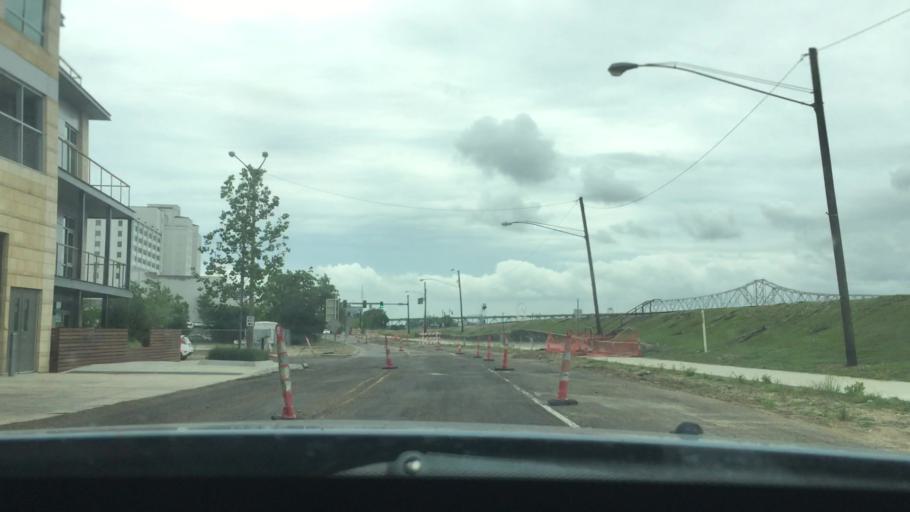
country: US
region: Louisiana
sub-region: West Baton Rouge Parish
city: Port Allen
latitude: 30.4518
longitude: -91.1905
